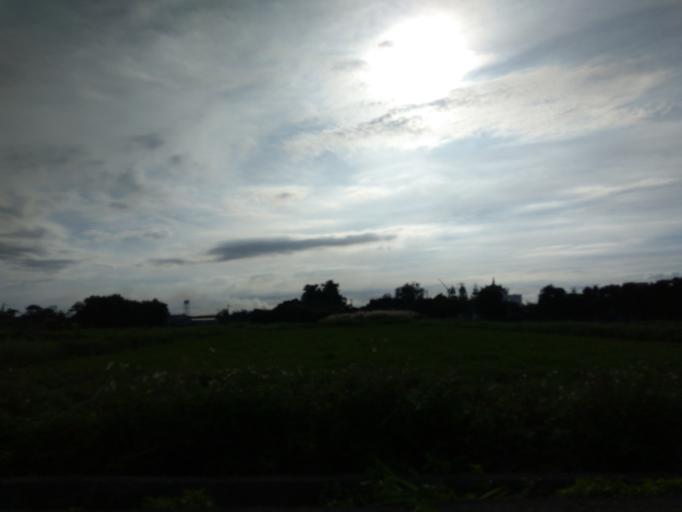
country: TW
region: Taiwan
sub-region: Hsinchu
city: Zhubei
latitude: 24.9419
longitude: 120.9914
